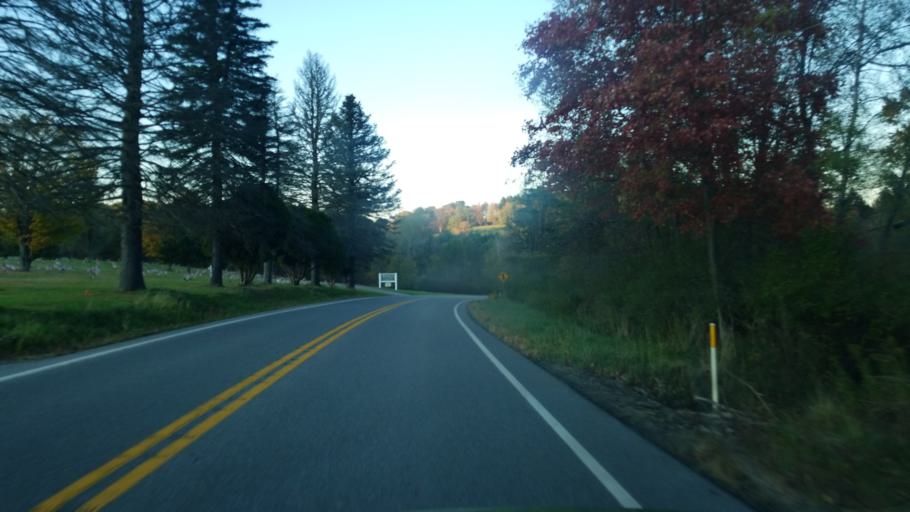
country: US
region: Pennsylvania
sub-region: Jefferson County
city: Reynoldsville
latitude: 41.0770
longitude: -78.9033
